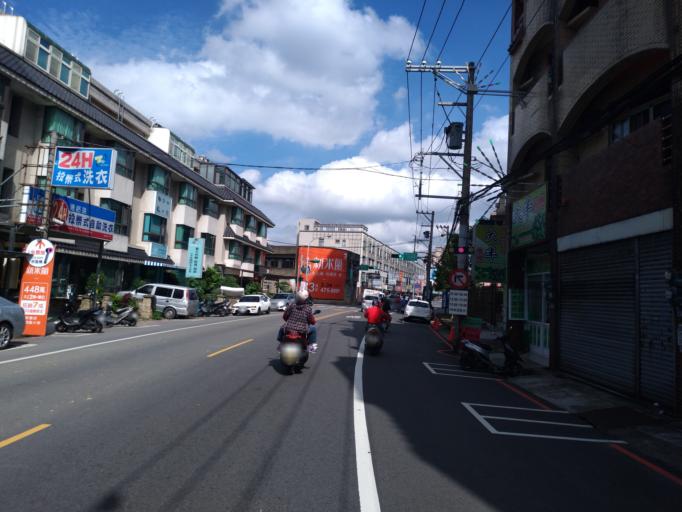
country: TW
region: Taiwan
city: Daxi
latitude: 24.9122
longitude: 121.1577
